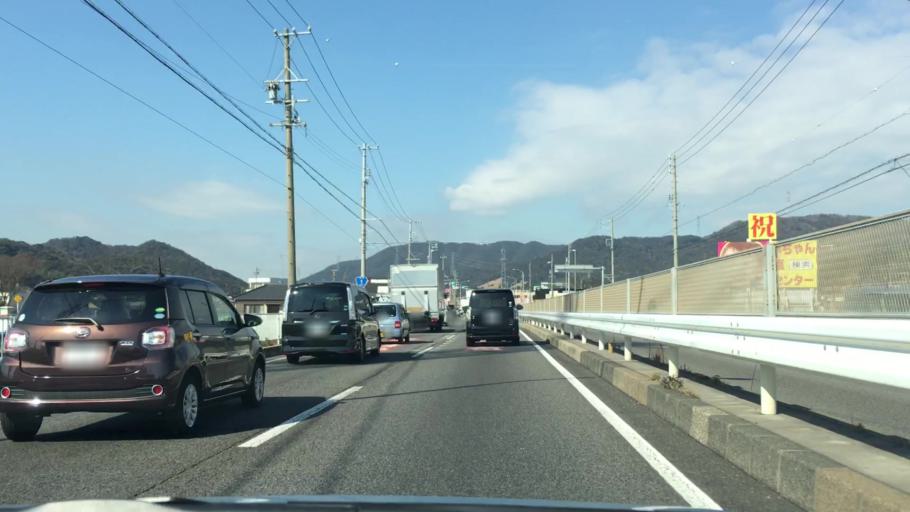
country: JP
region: Aichi
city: Kozakai-cho
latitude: 34.8526
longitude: 137.3155
